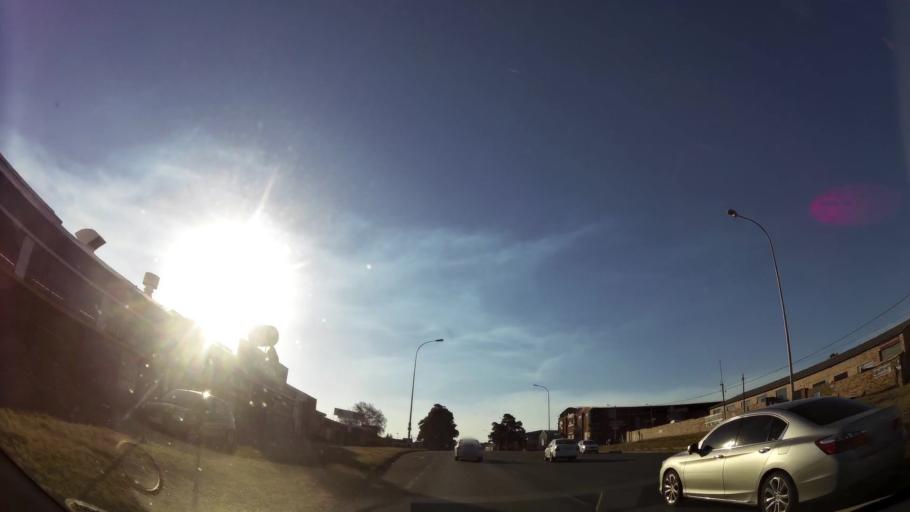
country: ZA
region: Gauteng
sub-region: City of Johannesburg Metropolitan Municipality
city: Roodepoort
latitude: -26.1483
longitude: 27.8631
